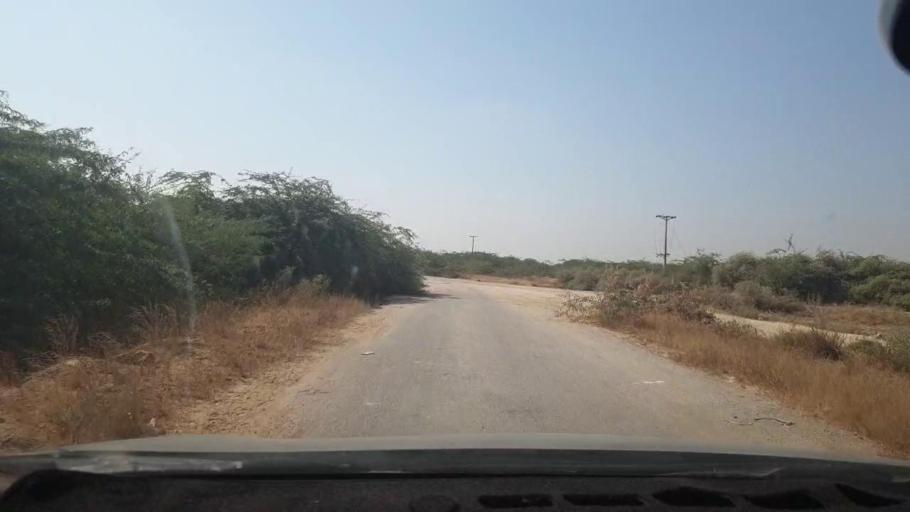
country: PK
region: Sindh
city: Malir Cantonment
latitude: 25.1541
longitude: 67.1356
